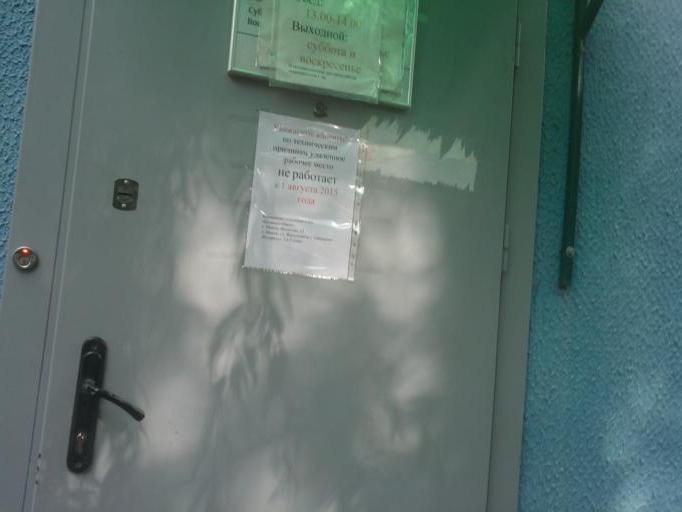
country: BY
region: Minsk
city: Minsk
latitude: 53.8739
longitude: 27.6199
